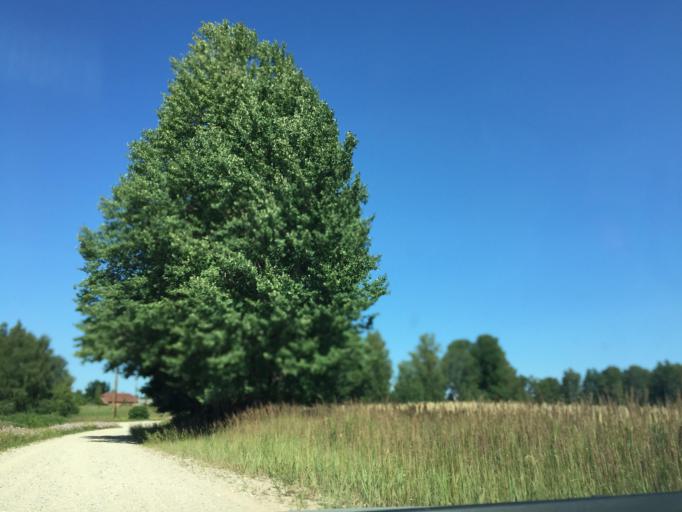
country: LV
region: Talsu Rajons
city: Stende
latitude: 57.1555
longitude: 22.2939
